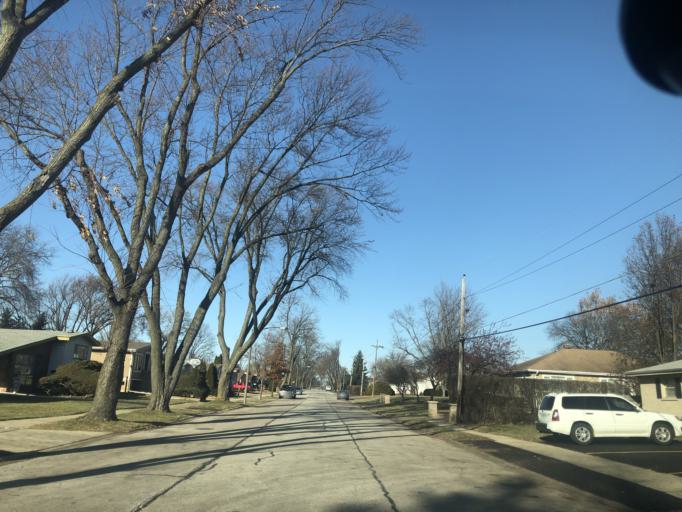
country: US
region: Illinois
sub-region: DuPage County
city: Addison
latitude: 41.9377
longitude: -87.9975
